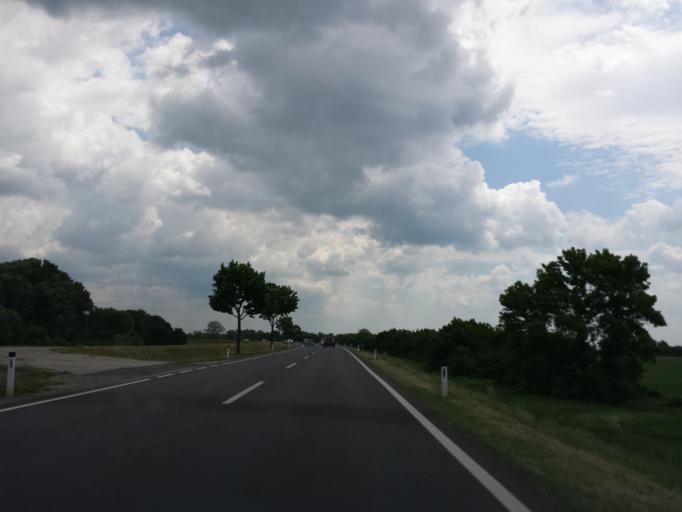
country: AT
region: Lower Austria
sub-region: Politischer Bezirk Bruck an der Leitha
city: Berg
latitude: 48.1224
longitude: 17.0437
